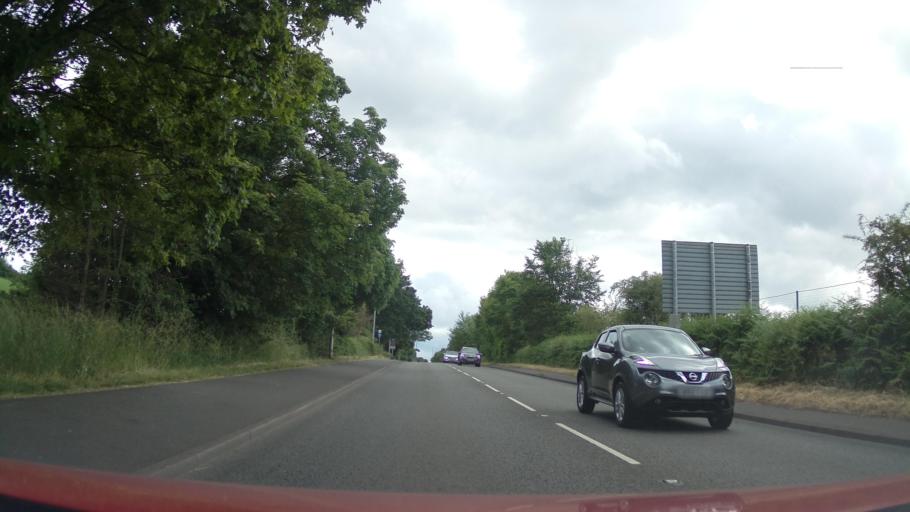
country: GB
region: England
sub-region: Dudley
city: Kingswinford
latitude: 52.4990
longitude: -2.1852
